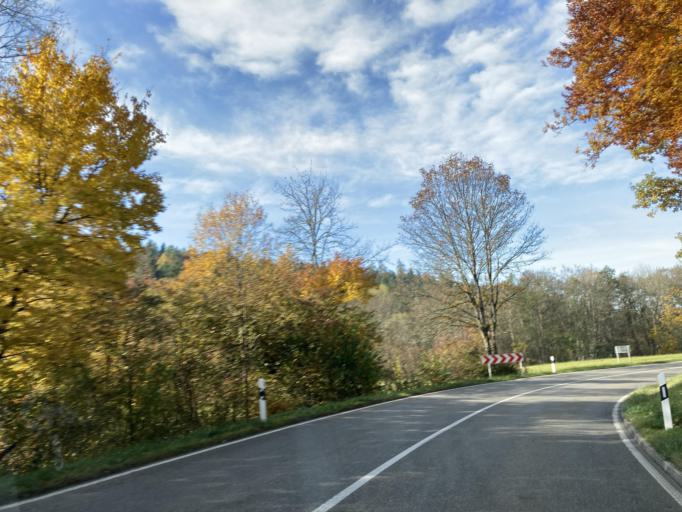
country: DE
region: Baden-Wuerttemberg
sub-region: Tuebingen Region
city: Bodelshausen
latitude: 48.4266
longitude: 8.9714
